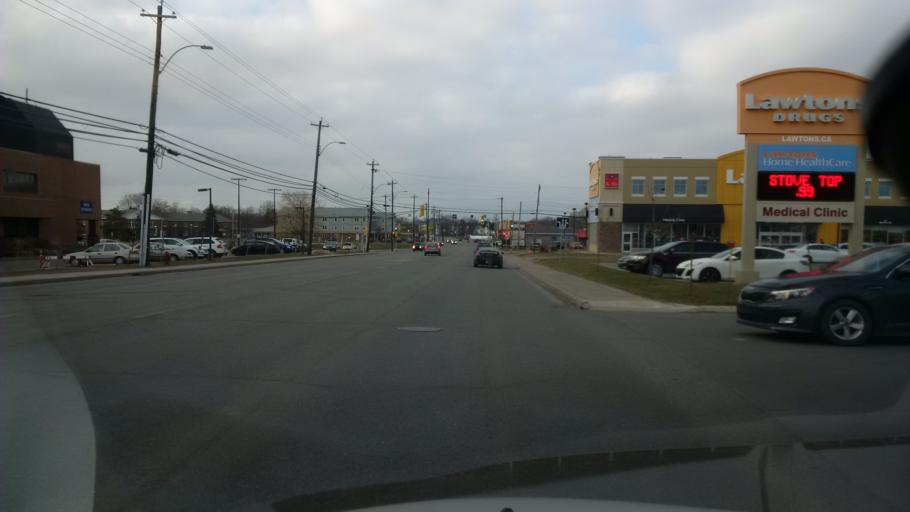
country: CA
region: Nova Scotia
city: New Glasgow
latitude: 45.5727
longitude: -62.6423
